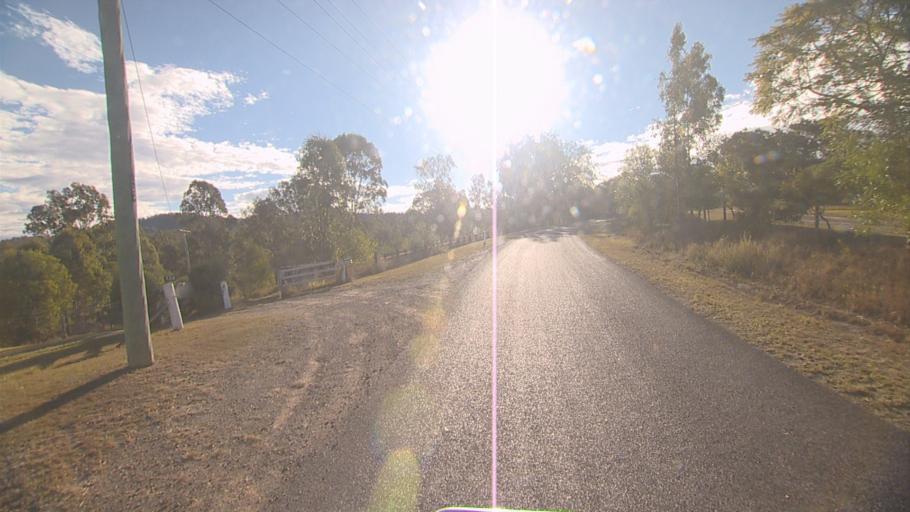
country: AU
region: Queensland
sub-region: Logan
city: Cedar Vale
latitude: -27.9270
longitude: 153.0680
